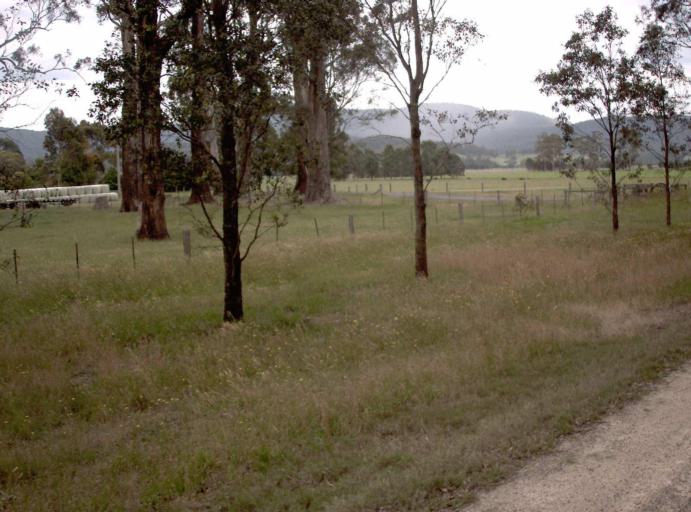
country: AU
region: New South Wales
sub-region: Bombala
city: Bombala
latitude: -37.5136
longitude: 149.1689
